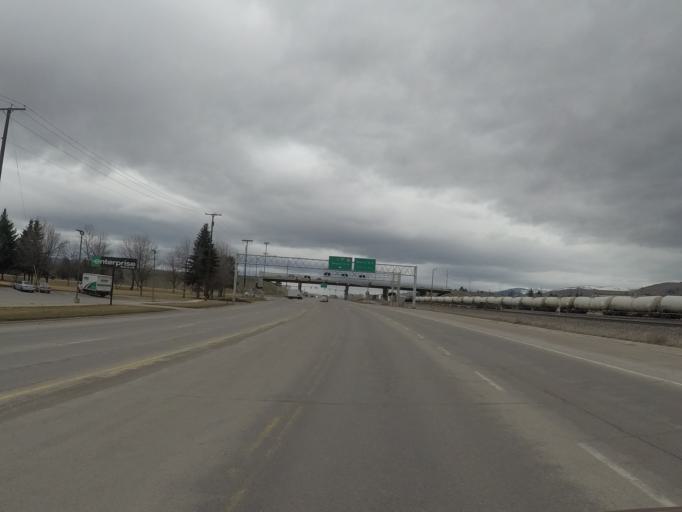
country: US
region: Montana
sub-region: Missoula County
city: Orchard Homes
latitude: 46.8971
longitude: -114.0355
